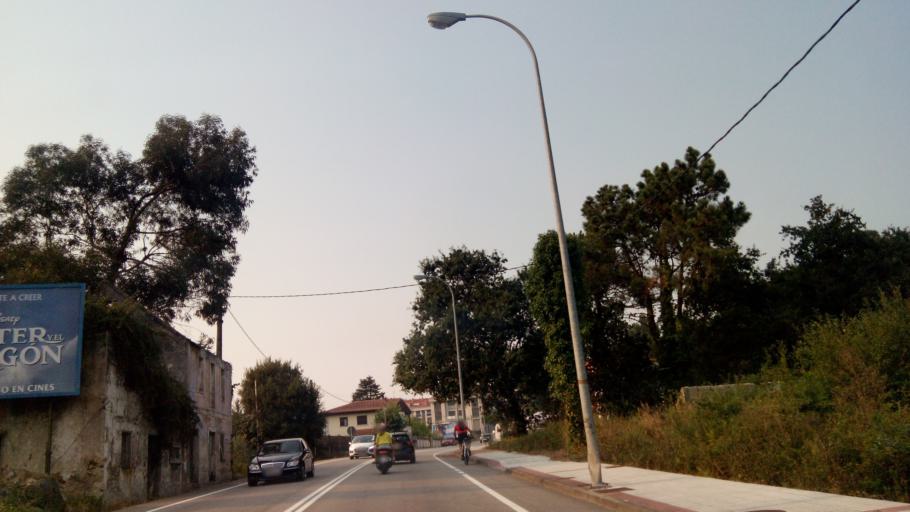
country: ES
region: Galicia
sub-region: Provincia de Pontevedra
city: Nigran
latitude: 42.1360
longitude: -8.8080
